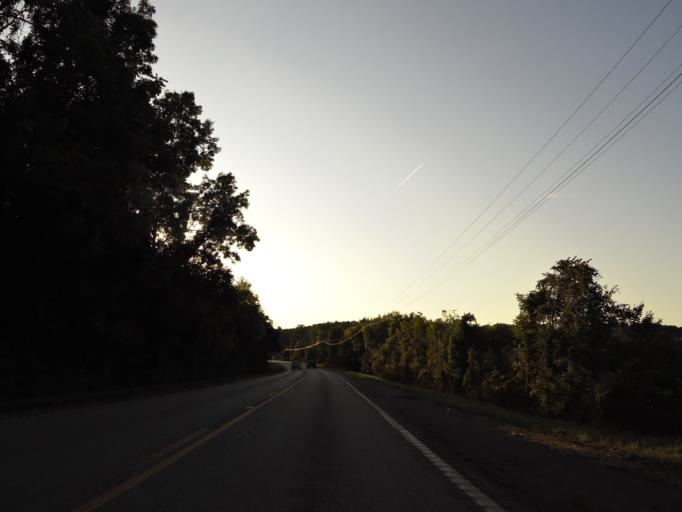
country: US
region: Tennessee
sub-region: Meigs County
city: Decatur
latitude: 35.6162
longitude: -84.7015
